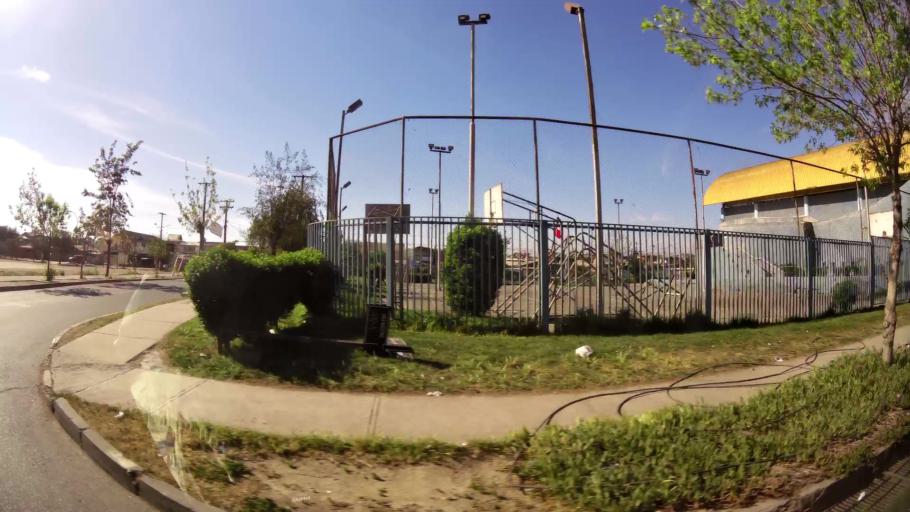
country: CL
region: Santiago Metropolitan
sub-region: Provincia de Santiago
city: Lo Prado
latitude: -33.5052
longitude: -70.7295
